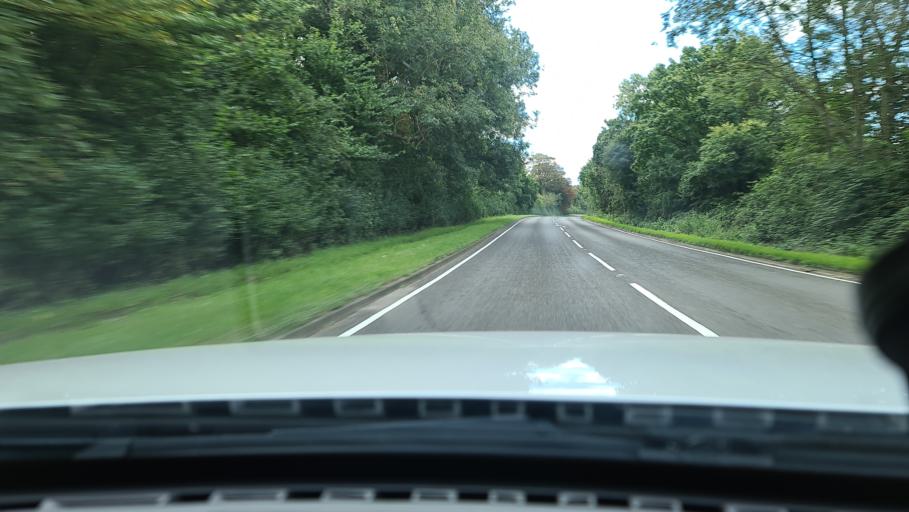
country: GB
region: England
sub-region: Warwickshire
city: Shipston on Stour
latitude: 52.0814
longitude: -1.6238
